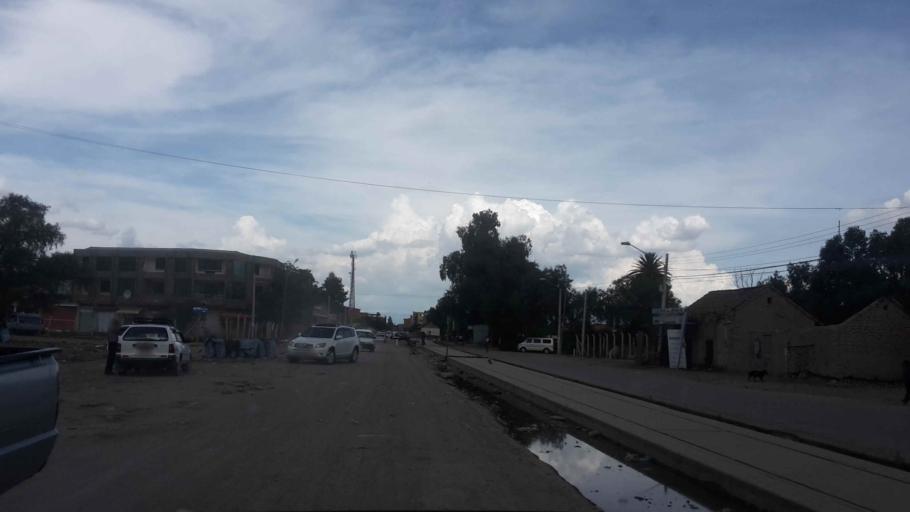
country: BO
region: Cochabamba
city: Sipe Sipe
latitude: -17.4020
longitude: -66.2852
